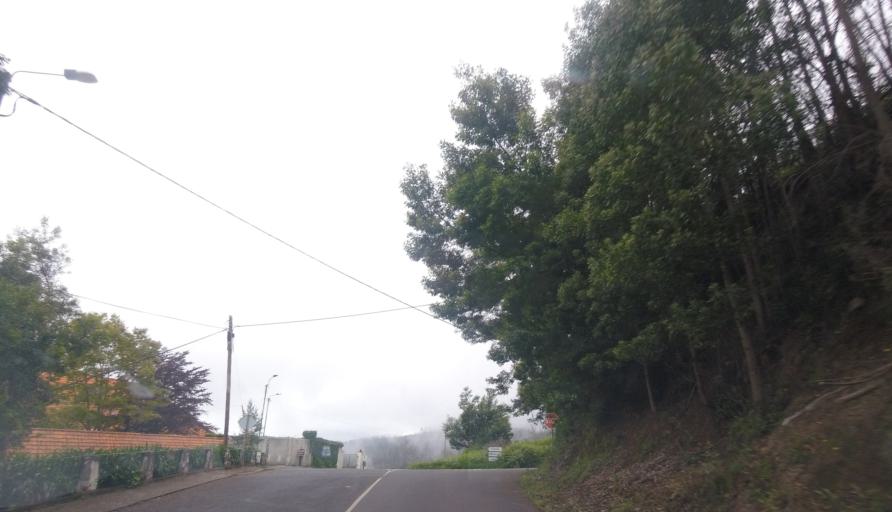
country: PT
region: Madeira
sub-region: Funchal
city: Nossa Senhora do Monte
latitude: 32.6853
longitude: -16.9004
